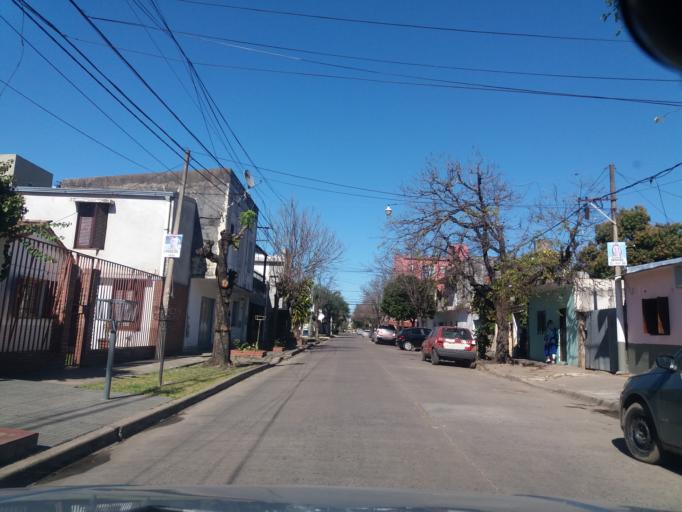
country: AR
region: Corrientes
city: Corrientes
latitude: -27.4742
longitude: -58.8197
